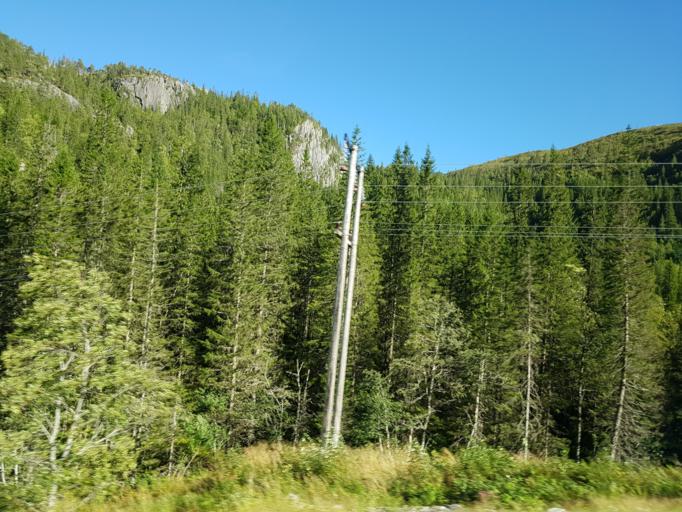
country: NO
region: Sor-Trondelag
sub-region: Afjord
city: A i Afjord
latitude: 63.7738
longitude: 10.2365
